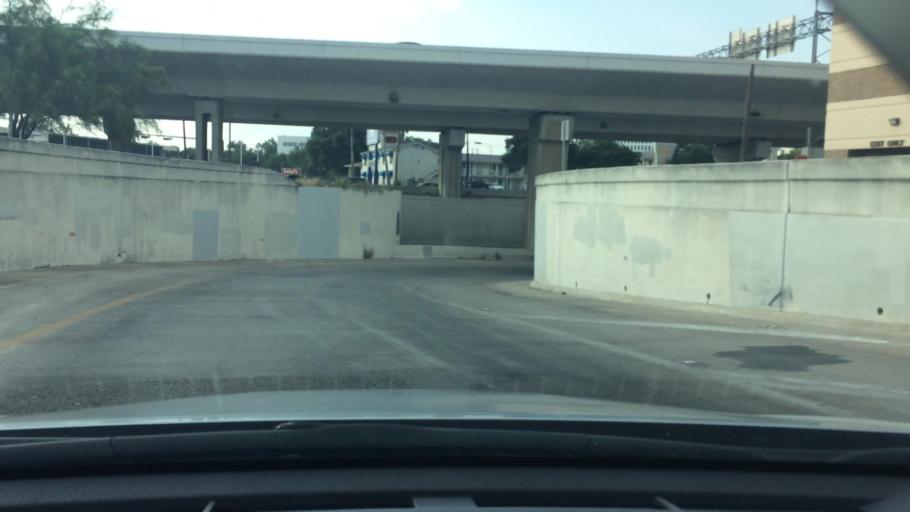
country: US
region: Texas
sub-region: Bexar County
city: San Antonio
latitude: 29.4354
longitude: -98.4934
